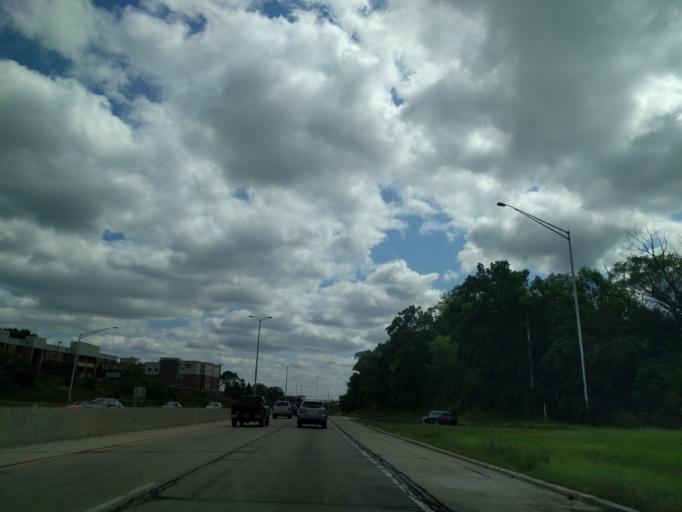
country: US
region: Wisconsin
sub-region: Milwaukee County
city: Fox Point
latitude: 43.1466
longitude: -87.9159
